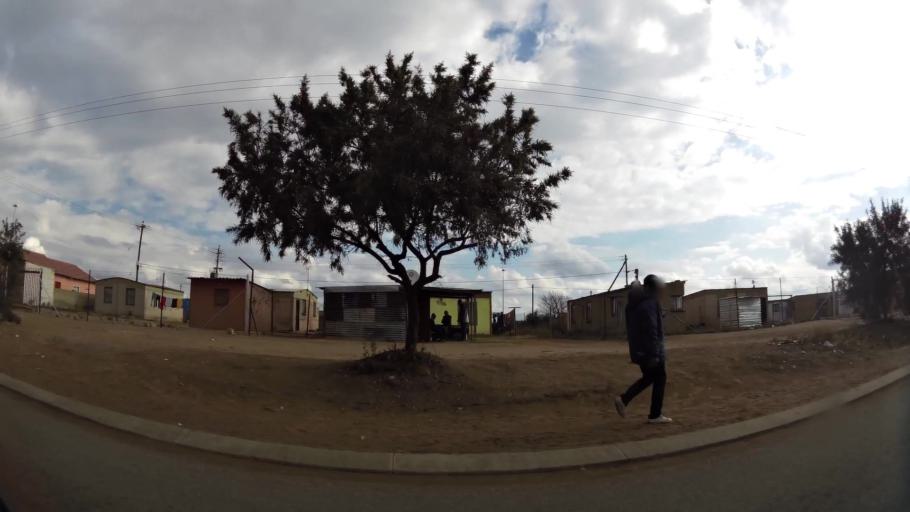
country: ZA
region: Gauteng
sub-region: Sedibeng District Municipality
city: Vanderbijlpark
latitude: -26.6834
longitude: 27.7821
